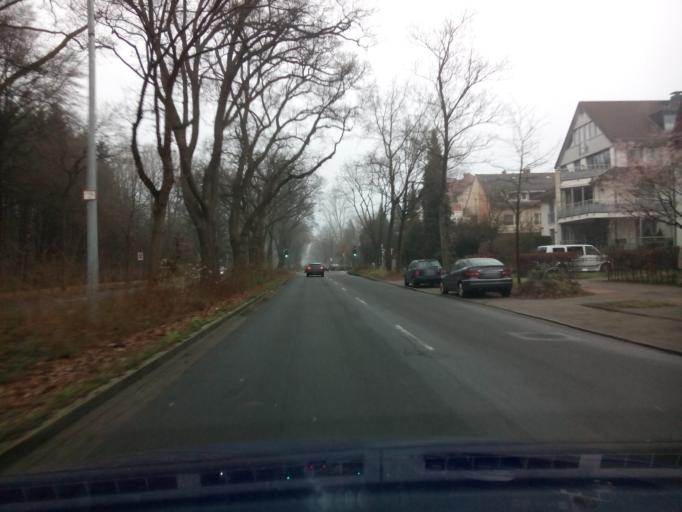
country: DE
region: Bremen
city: Bremen
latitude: 53.0935
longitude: 8.8328
